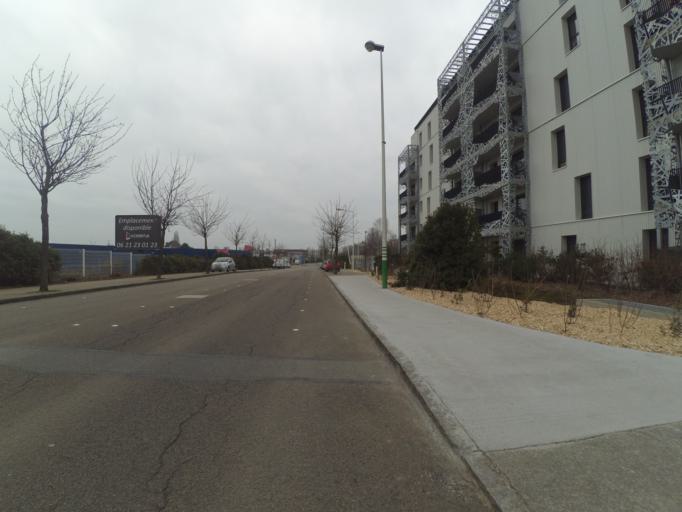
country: FR
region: Pays de la Loire
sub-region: Departement de la Loire-Atlantique
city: Saint-Herblain
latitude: 47.2199
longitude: -1.6402
